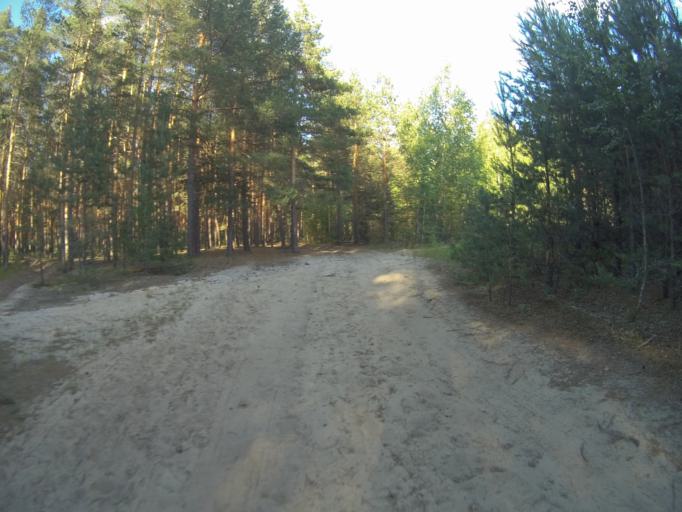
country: RU
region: Vladimir
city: Kommunar
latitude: 56.0965
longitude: 40.4626
